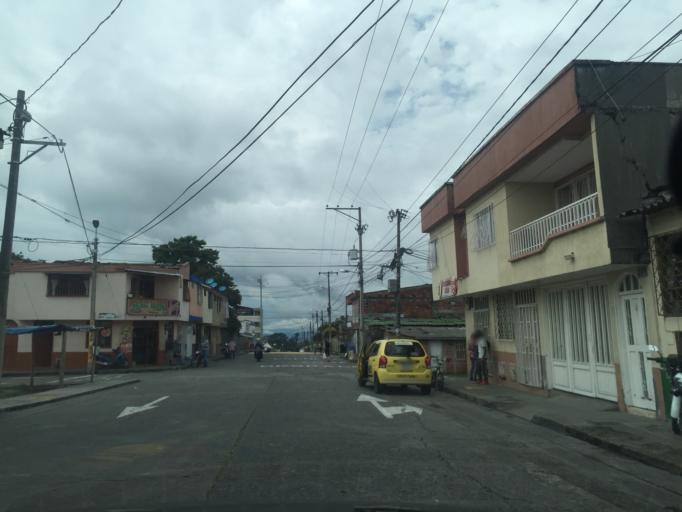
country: CO
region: Quindio
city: Armenia
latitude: 4.5309
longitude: -75.6830
